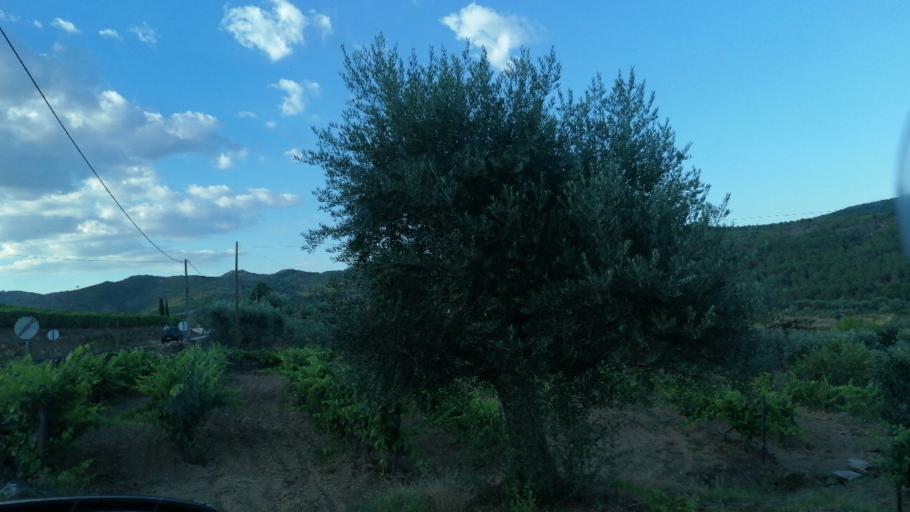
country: PT
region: Viseu
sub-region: Sao Joao da Pesqueira
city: Sao Joao da Pesqueira
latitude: 41.2567
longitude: -7.4410
